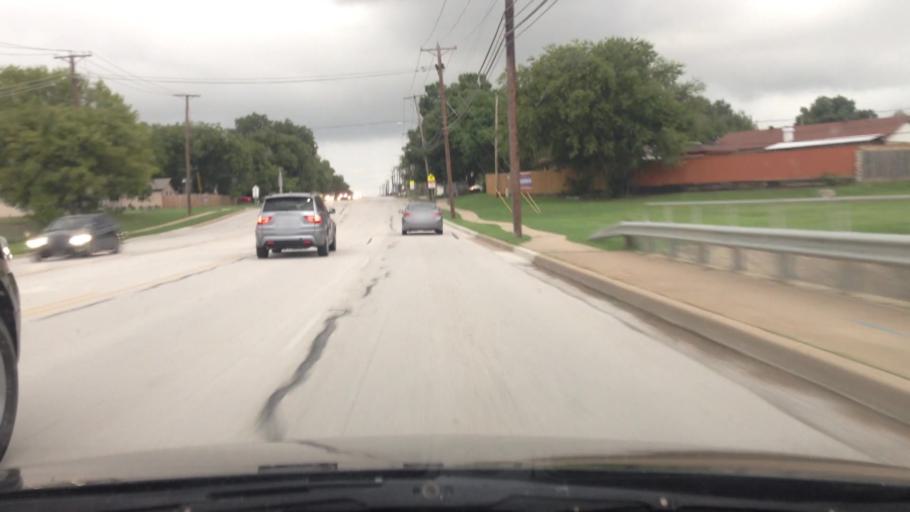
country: US
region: Texas
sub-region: Tarrant County
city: Watauga
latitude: 32.8604
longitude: -97.2476
